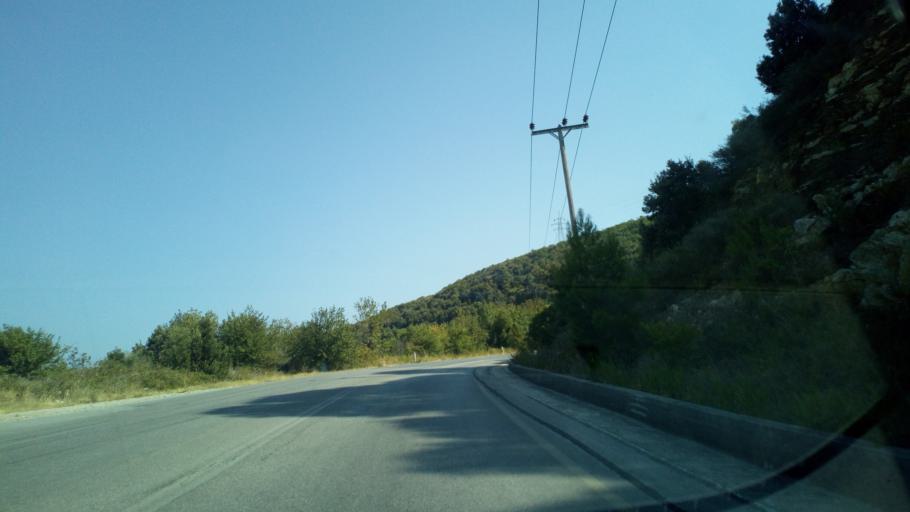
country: GR
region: Central Macedonia
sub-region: Nomos Thessalonikis
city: Stavros
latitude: 40.6572
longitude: 23.7347
